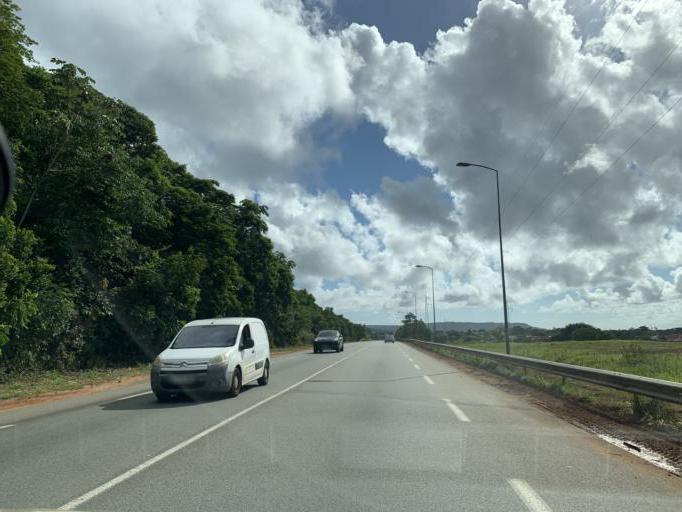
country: GF
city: Macouria
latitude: 4.8916
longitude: -52.3435
